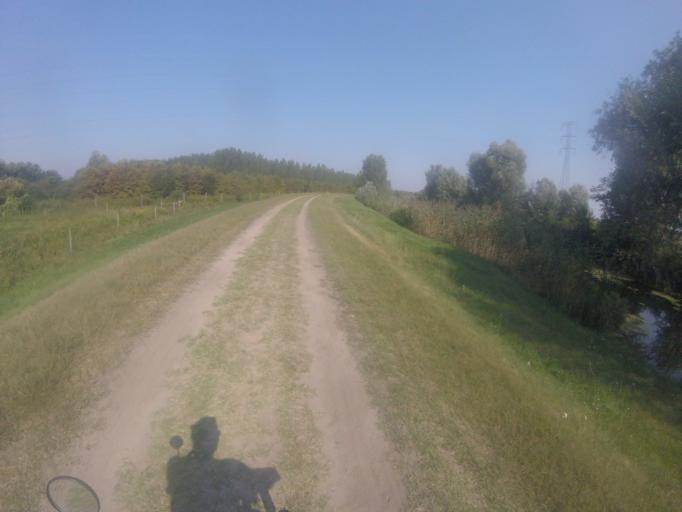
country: HU
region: Bacs-Kiskun
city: Baja
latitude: 46.2157
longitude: 18.9550
